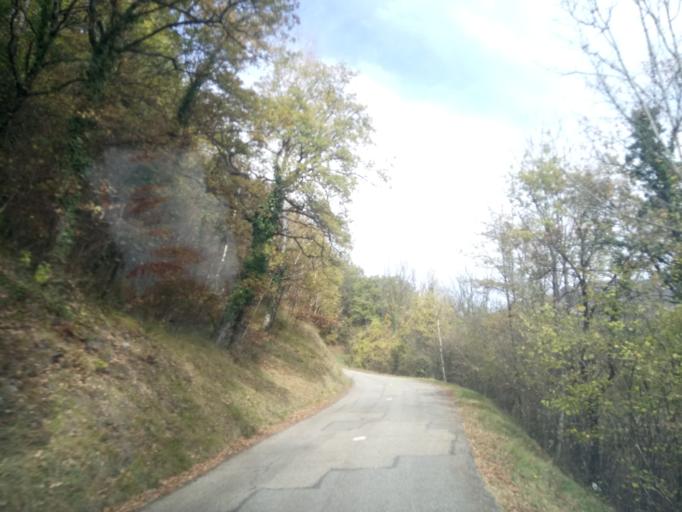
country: FR
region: Rhone-Alpes
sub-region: Departement de la Savoie
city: La Chambre
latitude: 45.3739
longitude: 6.3089
